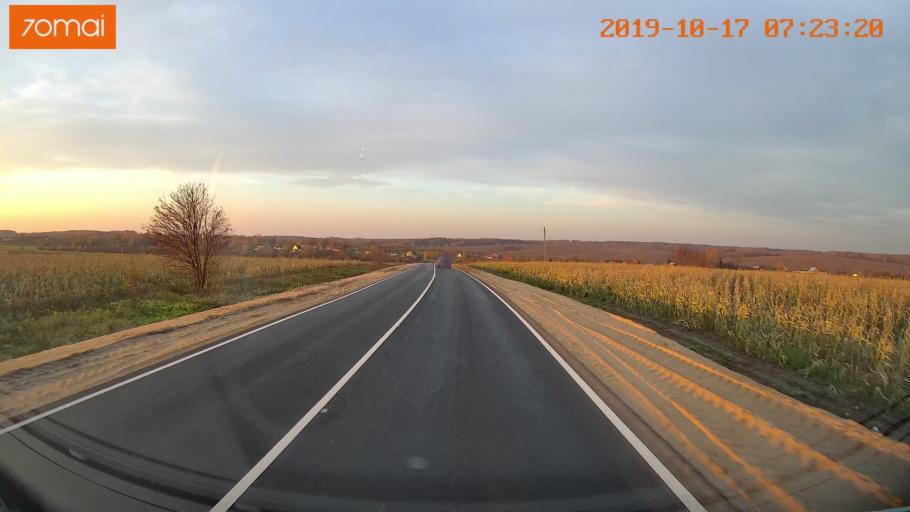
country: RU
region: Ivanovo
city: Gavrilov Posad
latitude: 56.3355
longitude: 40.1221
